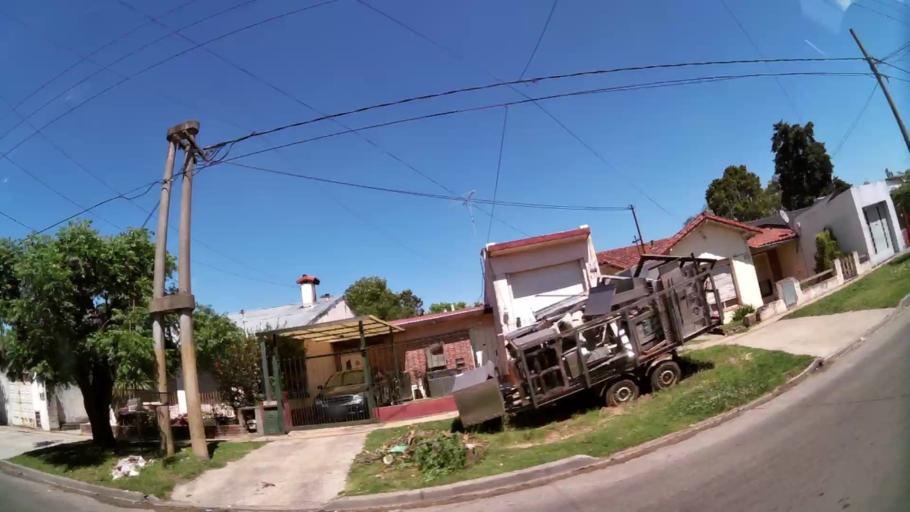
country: AR
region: Buenos Aires
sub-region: Partido de Tigre
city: Tigre
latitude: -34.4883
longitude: -58.6475
